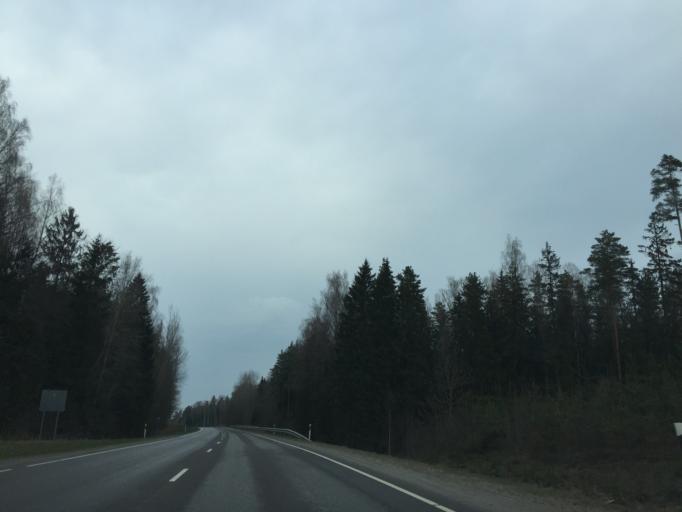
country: EE
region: Tartu
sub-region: UElenurme vald
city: Ulenurme
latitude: 58.1023
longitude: 26.7403
